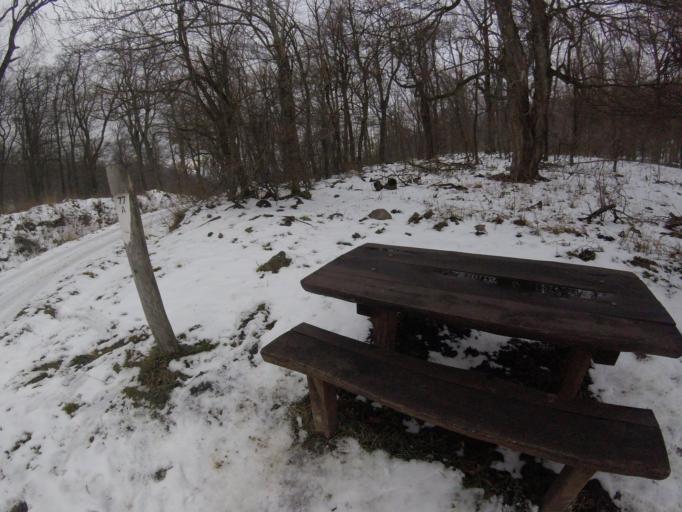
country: HU
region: Pest
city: Dunabogdany
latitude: 47.7578
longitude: 19.0087
